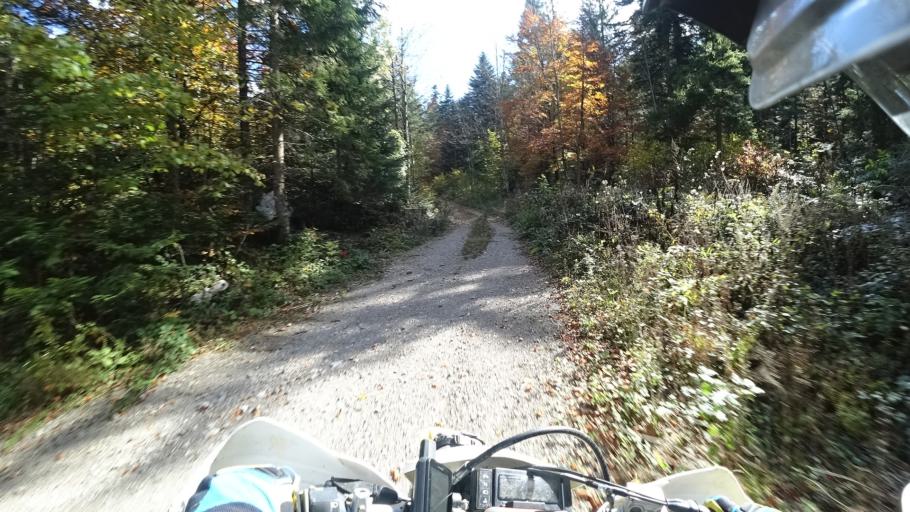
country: HR
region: Karlovacka
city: Plaski
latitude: 45.0654
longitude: 15.3196
